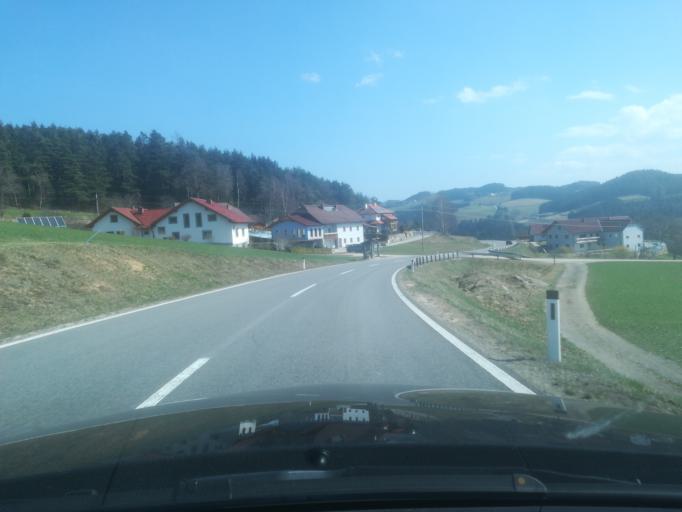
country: AT
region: Upper Austria
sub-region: Politischer Bezirk Perg
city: Sankt Georgen am Walde
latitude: 48.4176
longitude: 14.7578
